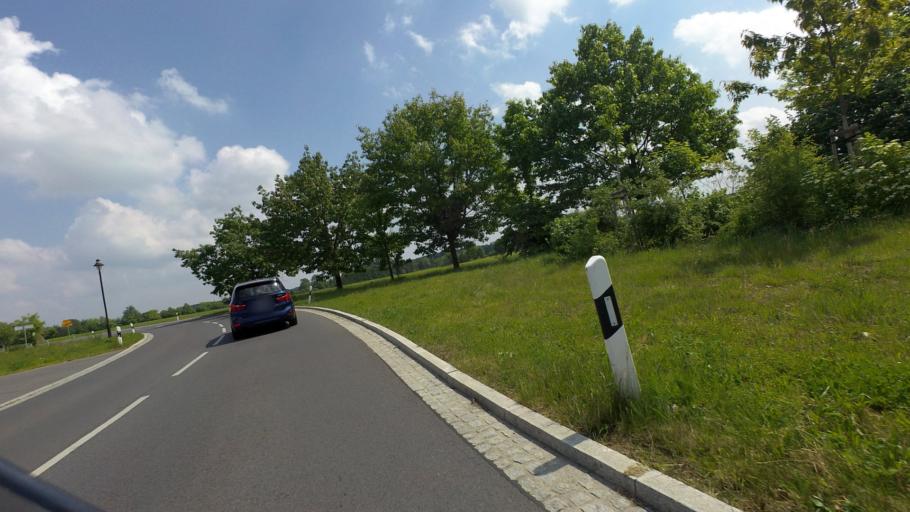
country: DE
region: Saxony
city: Schleife
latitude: 51.5468
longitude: 14.5472
